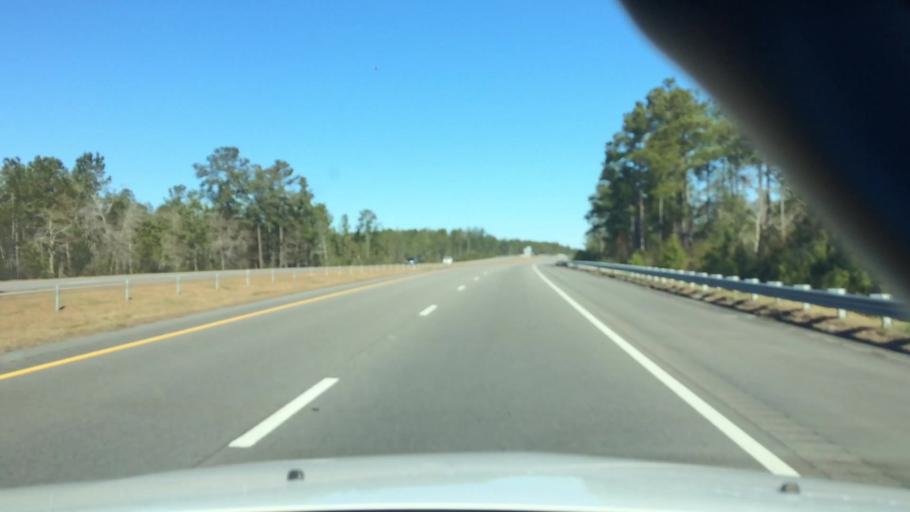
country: US
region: North Carolina
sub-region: Brunswick County
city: Leland
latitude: 34.2138
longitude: -78.0765
